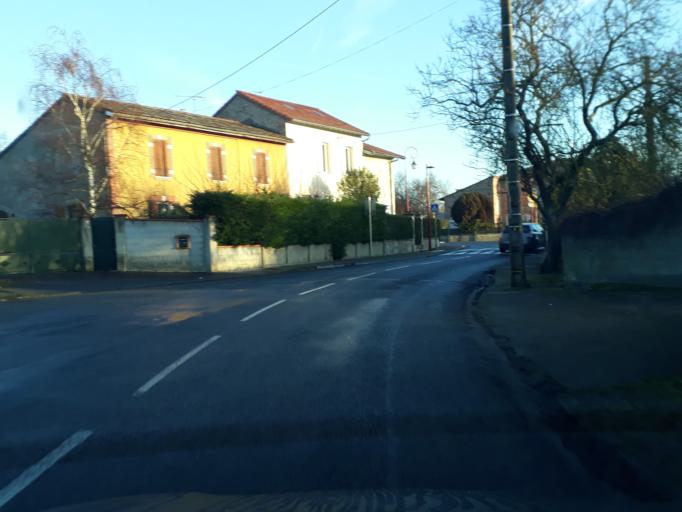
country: FR
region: Midi-Pyrenees
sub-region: Departement de la Haute-Garonne
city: Longages
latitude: 43.3528
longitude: 1.2366
